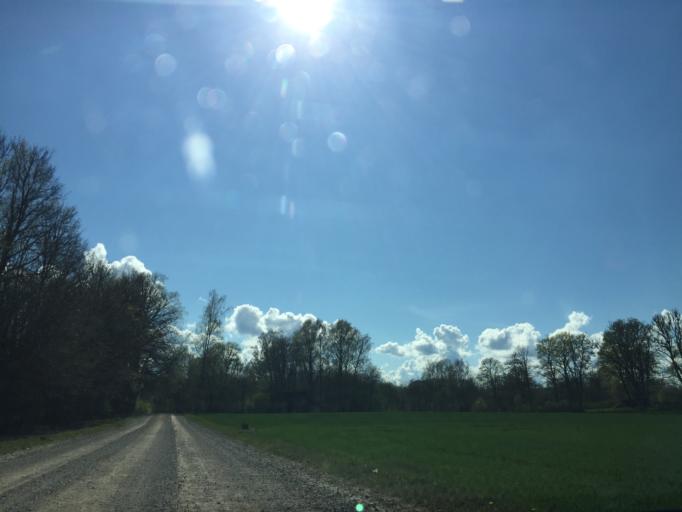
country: LV
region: Strenci
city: Strenci
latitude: 57.5057
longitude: 25.6631
